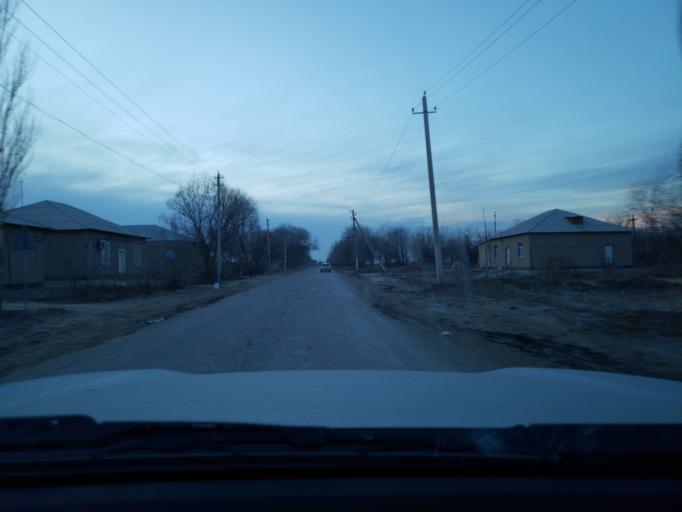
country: TM
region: Dasoguz
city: Tagta
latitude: 41.5848
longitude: 60.0587
